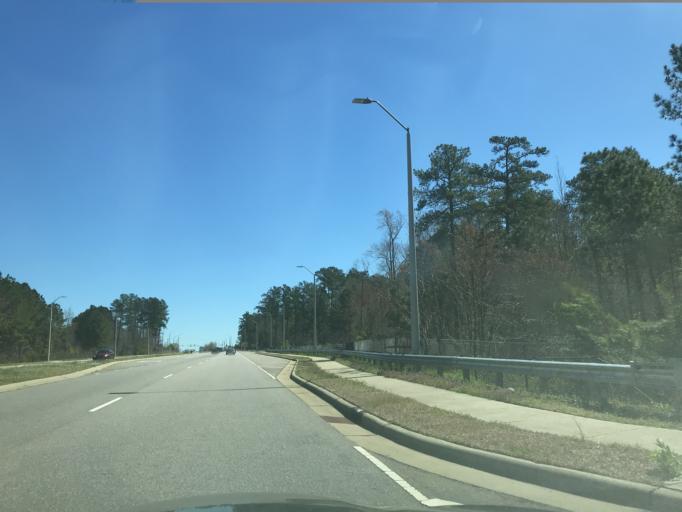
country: US
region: North Carolina
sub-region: Wake County
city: Garner
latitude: 35.6882
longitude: -78.5882
